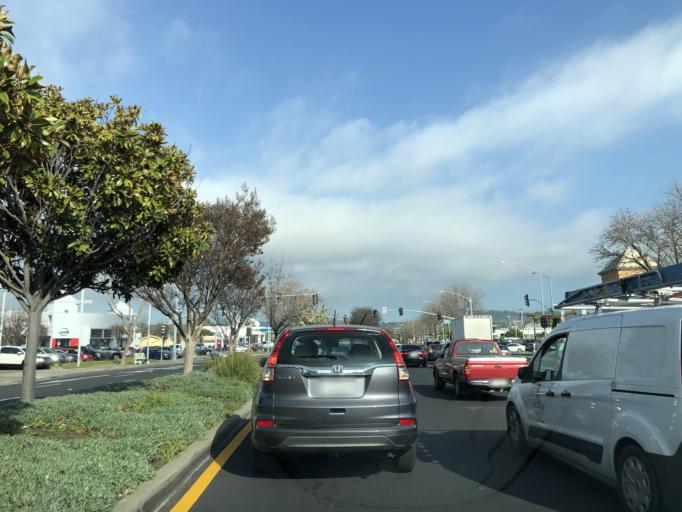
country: US
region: California
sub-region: Alameda County
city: San Leandro
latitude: 37.7118
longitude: -122.1633
